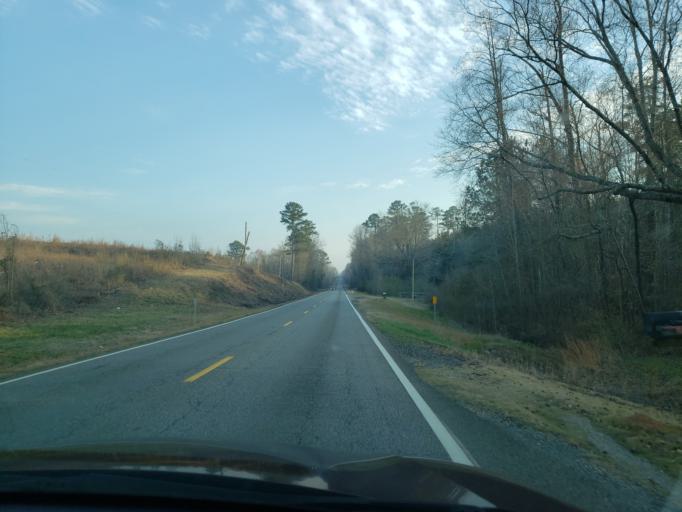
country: US
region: Alabama
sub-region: Hale County
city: Greensboro
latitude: 32.8039
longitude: -87.5934
